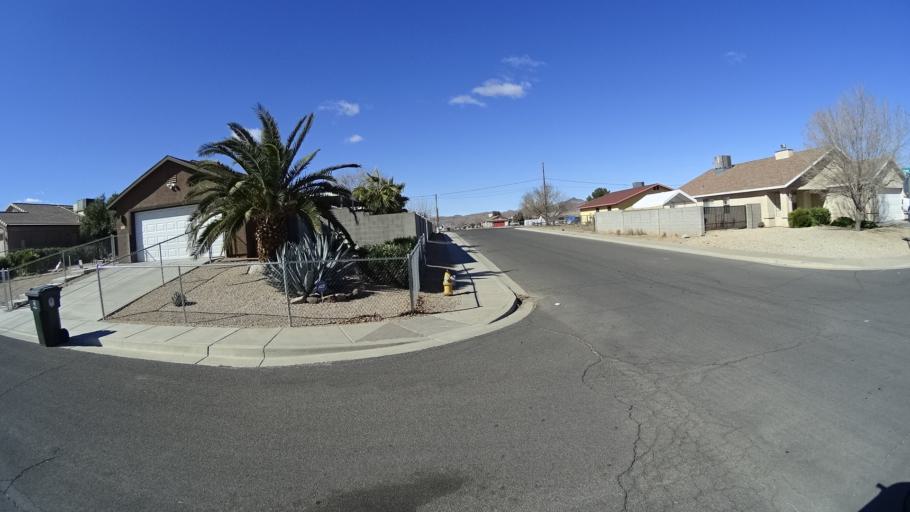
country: US
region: Arizona
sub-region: Mohave County
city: New Kingman-Butler
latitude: 35.2192
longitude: -113.9985
